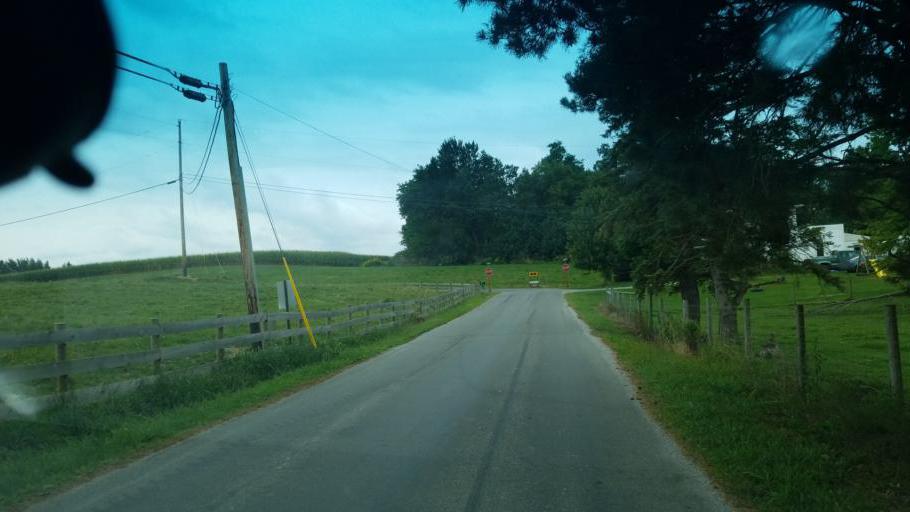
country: US
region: Ohio
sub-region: Richland County
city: Shelby
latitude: 40.9390
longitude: -82.6001
